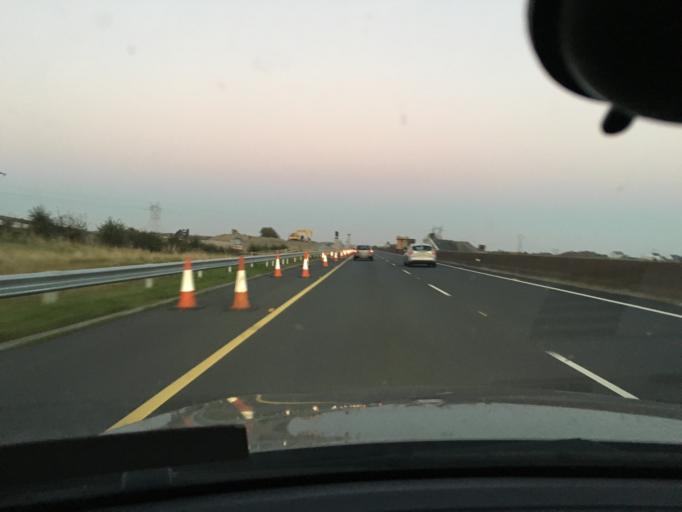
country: IE
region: Connaught
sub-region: County Galway
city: Athenry
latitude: 53.2976
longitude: -8.8124
